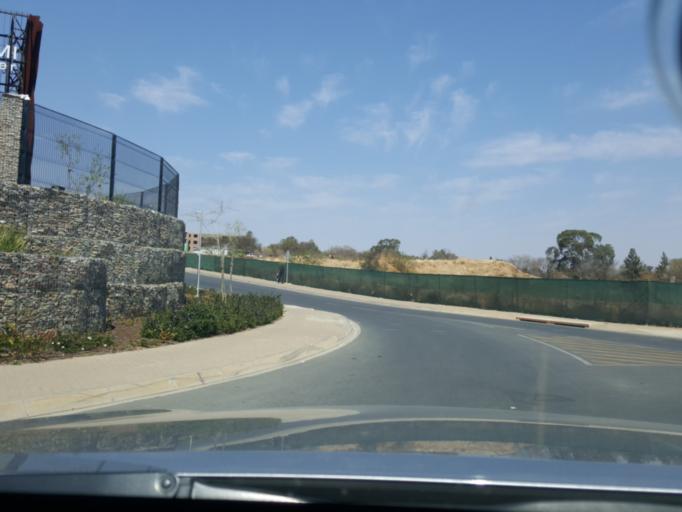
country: ZA
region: Gauteng
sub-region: City of Johannesburg Metropolitan Municipality
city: Midrand
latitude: -25.9838
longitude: 28.0740
